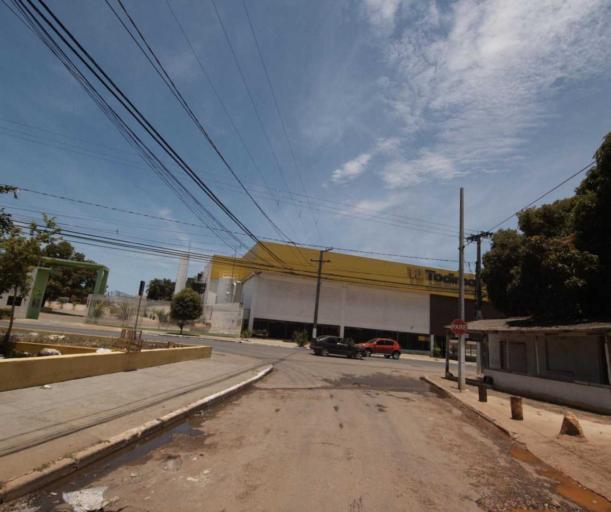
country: BR
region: Mato Grosso
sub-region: Cuiaba
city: Cuiaba
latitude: -15.6051
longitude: -56.1257
